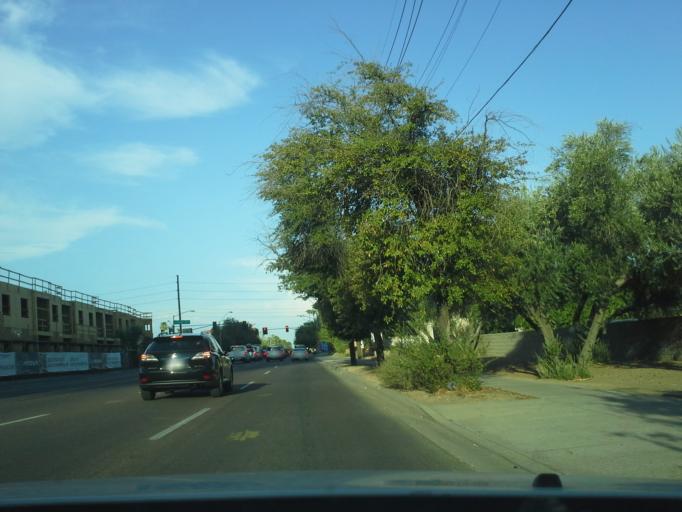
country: US
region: Arizona
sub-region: Maricopa County
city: Phoenix
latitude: 33.4802
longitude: -112.0708
